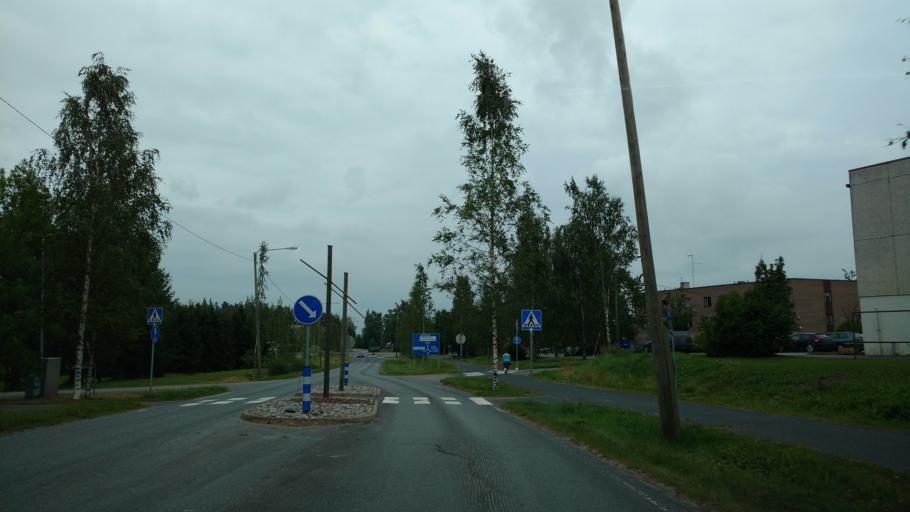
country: FI
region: Haeme
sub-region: Forssa
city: Ypaejae
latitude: 60.8054
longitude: 23.2792
